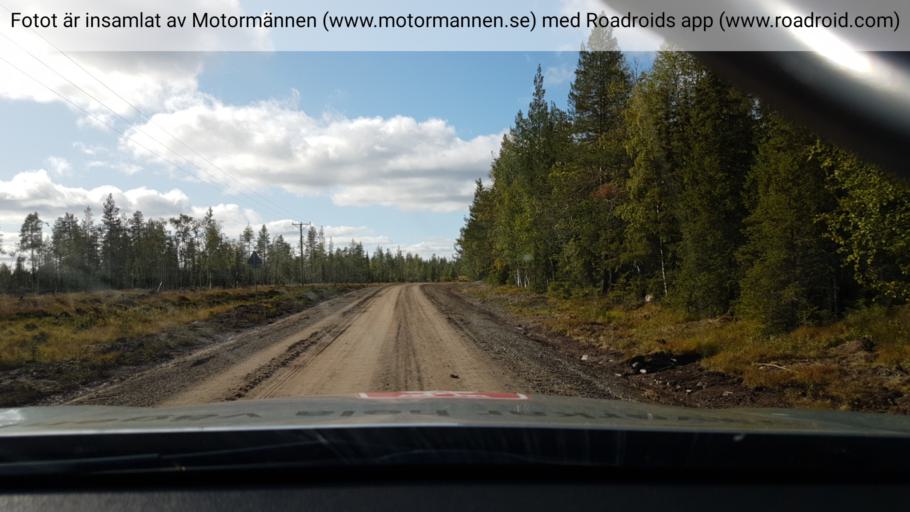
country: SE
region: Vaesterbotten
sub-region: Mala Kommun
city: Mala
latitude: 65.3741
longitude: 18.5947
